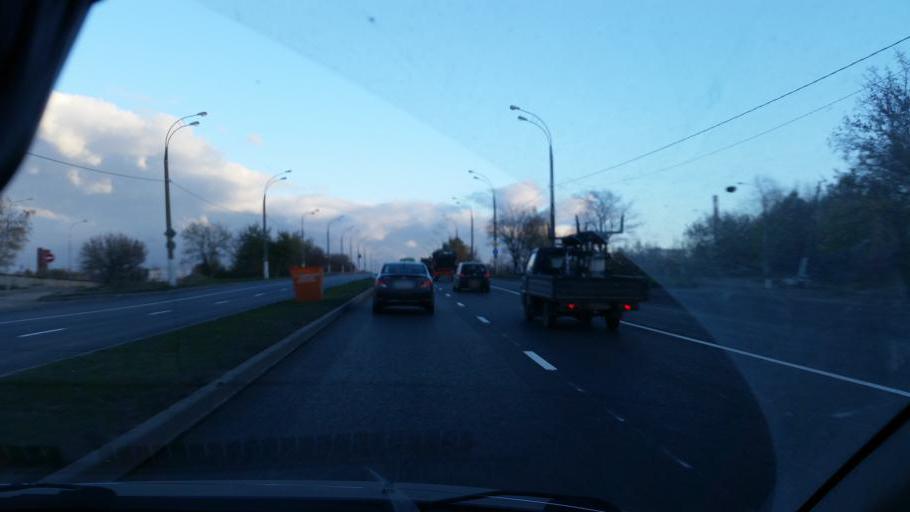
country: RU
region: Moskovskaya
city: Biryulevo Zapadnoye
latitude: 55.6060
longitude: 37.6279
